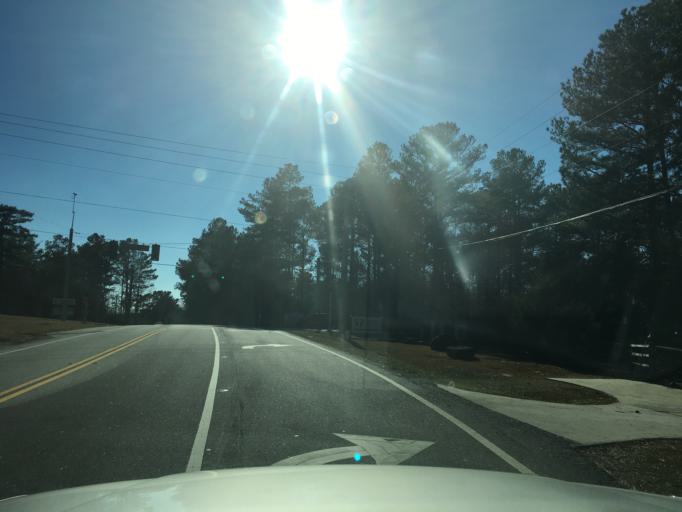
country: US
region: Georgia
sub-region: Carroll County
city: Villa Rica
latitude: 33.7114
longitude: -84.8418
